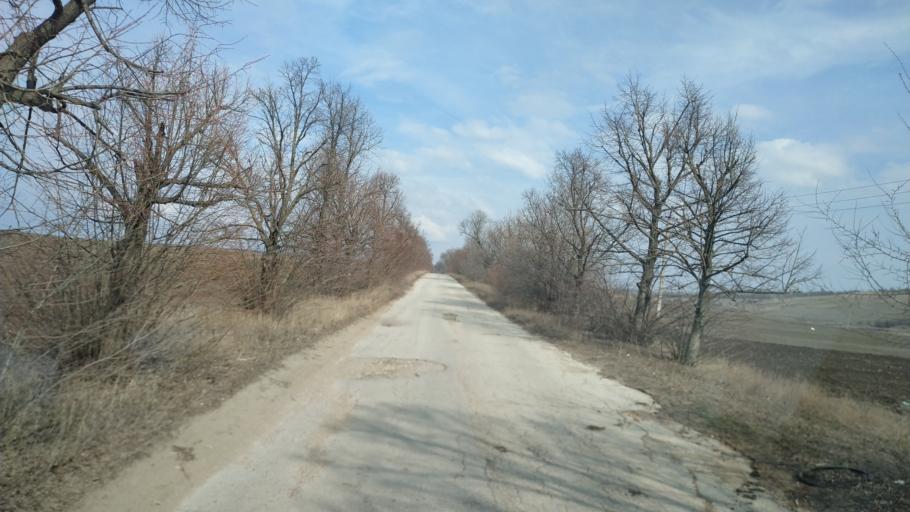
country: MD
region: Anenii Noi
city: Anenii Noi
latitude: 46.9363
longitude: 29.1078
